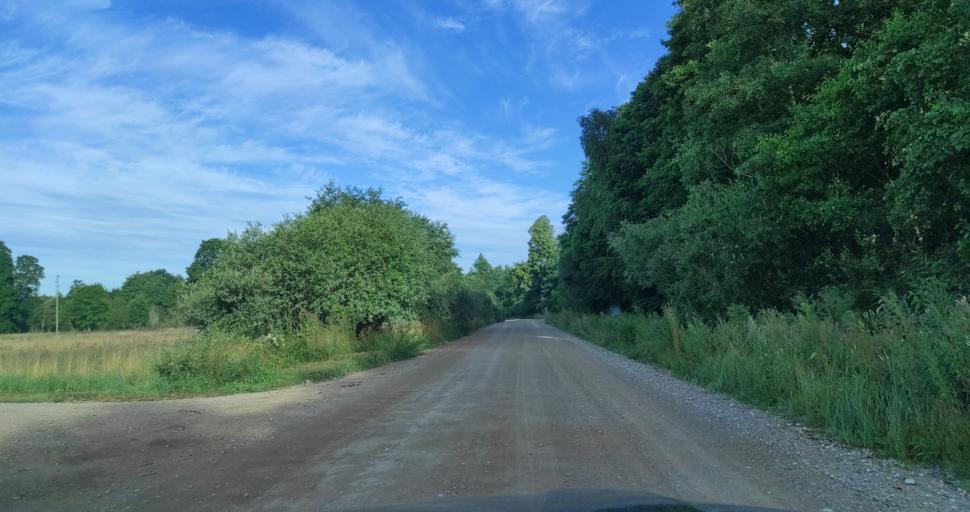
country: LV
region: Durbe
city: Liegi
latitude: 56.7517
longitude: 21.3599
